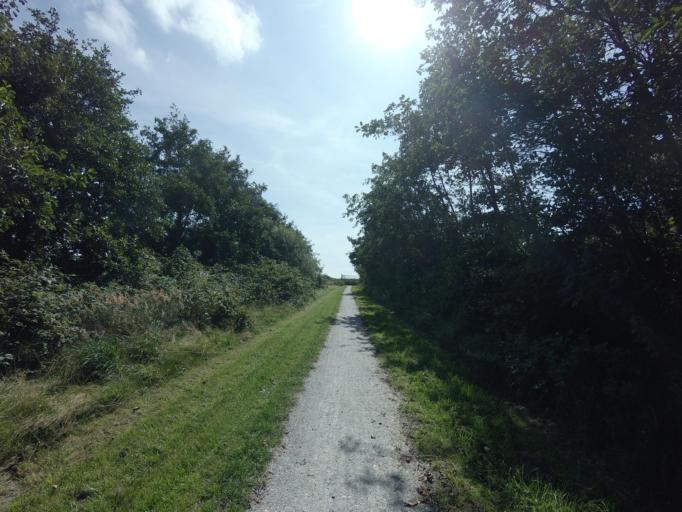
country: NL
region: Friesland
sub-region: Gemeente Ameland
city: Hollum
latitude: 53.4509
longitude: 5.6480
